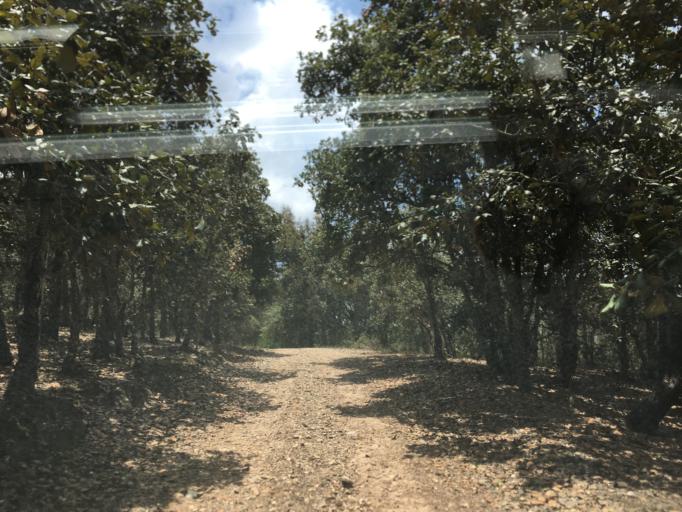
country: MX
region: Oaxaca
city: San Andres Sinaxtla
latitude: 17.6058
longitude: -97.2666
